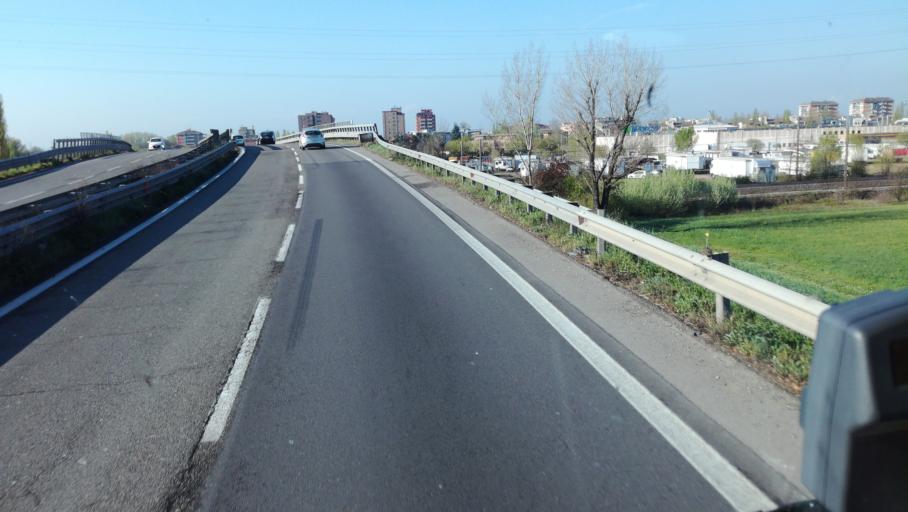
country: IT
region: Emilia-Romagna
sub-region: Provincia di Modena
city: Modena
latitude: 44.6457
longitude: 10.9617
